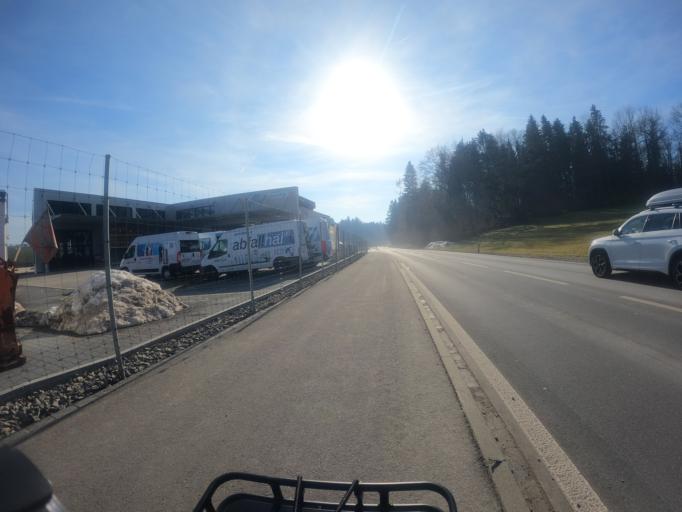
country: CH
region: Zurich
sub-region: Bezirk Affoltern
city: Knonau
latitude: 47.2136
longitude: 8.4679
